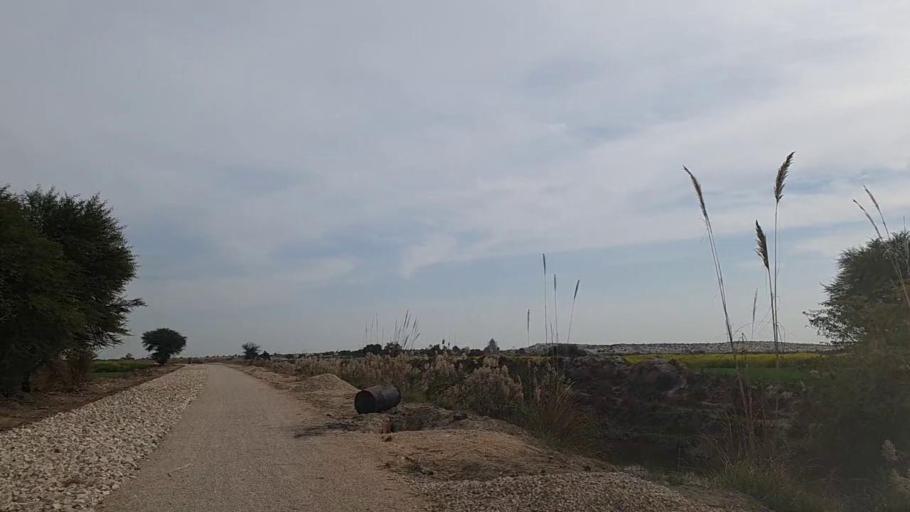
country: PK
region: Sindh
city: Jam Sahib
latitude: 26.4054
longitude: 68.4949
